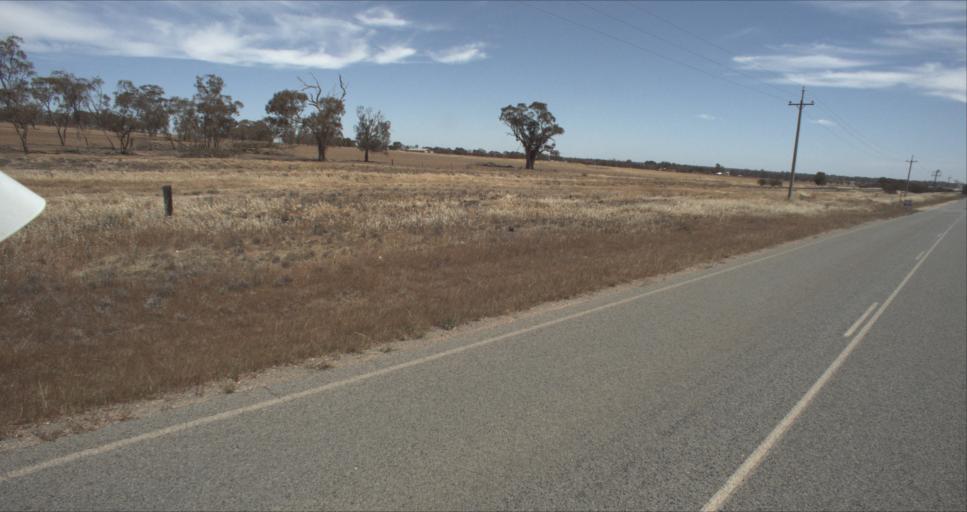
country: AU
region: New South Wales
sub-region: Leeton
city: Leeton
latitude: -34.6181
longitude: 146.4412
